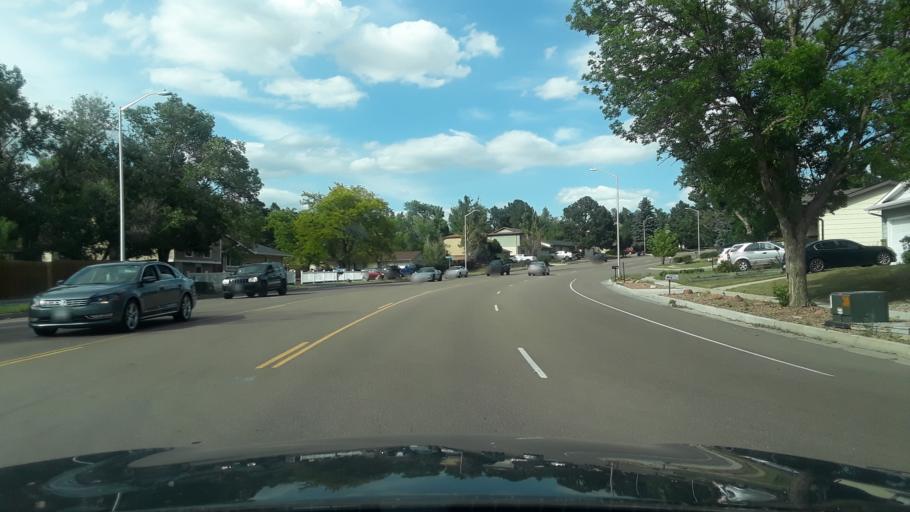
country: US
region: Colorado
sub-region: El Paso County
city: Cimarron Hills
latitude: 38.8851
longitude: -104.7497
